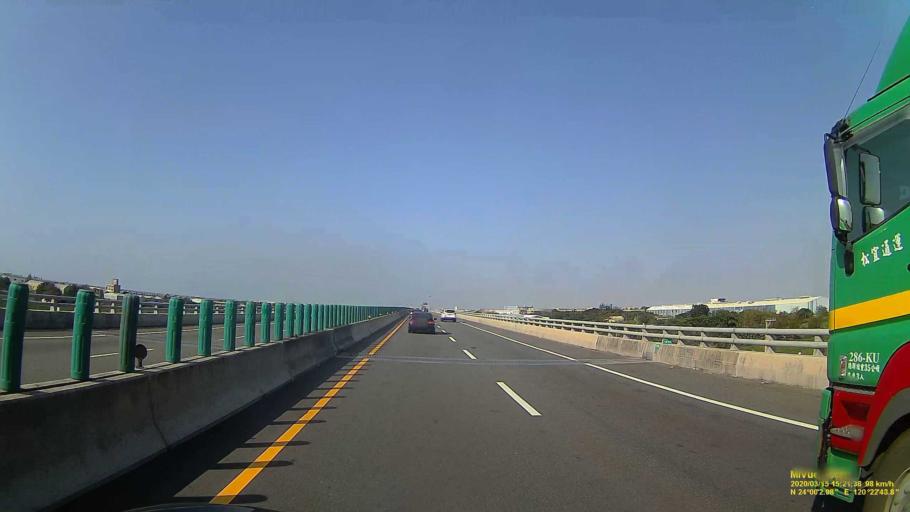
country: TW
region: Taiwan
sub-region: Changhua
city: Chang-hua
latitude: 24.0010
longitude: 120.3806
